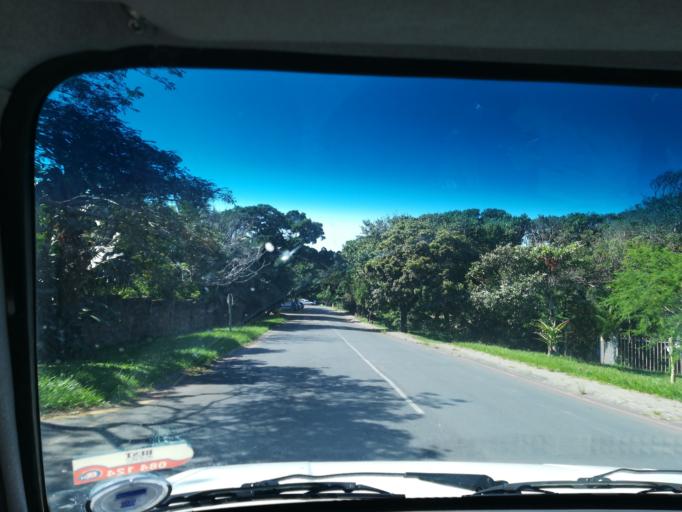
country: ZA
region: KwaZulu-Natal
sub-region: Ugu District Municipality
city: Scottburgh
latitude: -30.3852
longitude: 30.6942
